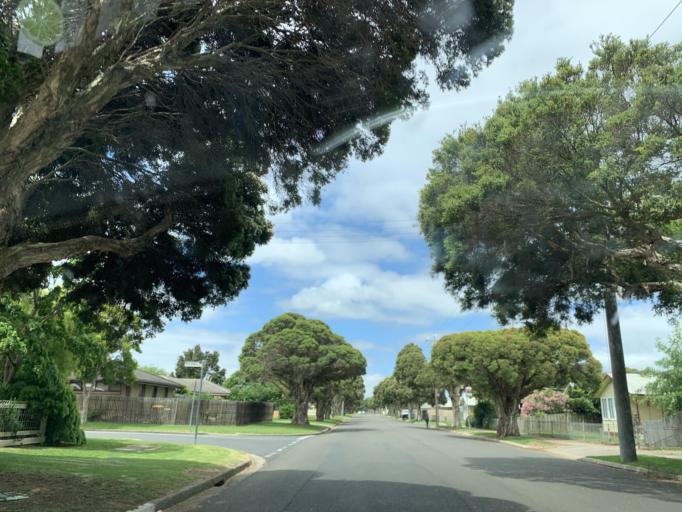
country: AU
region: Victoria
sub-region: Wellington
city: Sale
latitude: -38.1044
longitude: 147.0844
